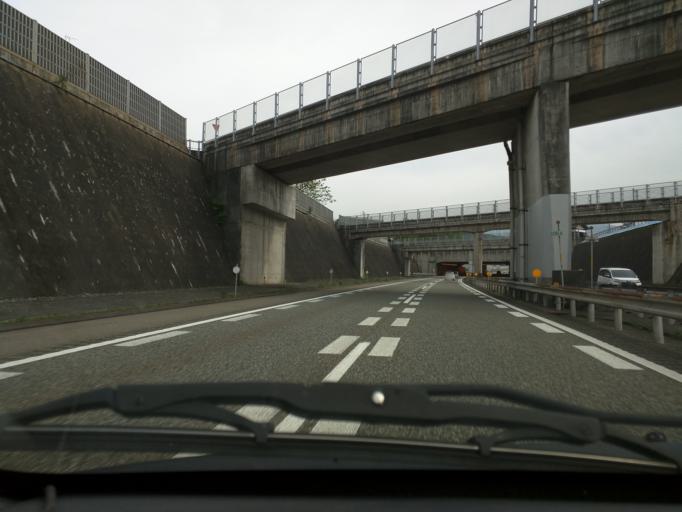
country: JP
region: Niigata
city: Ojiya
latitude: 37.2330
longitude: 138.9757
